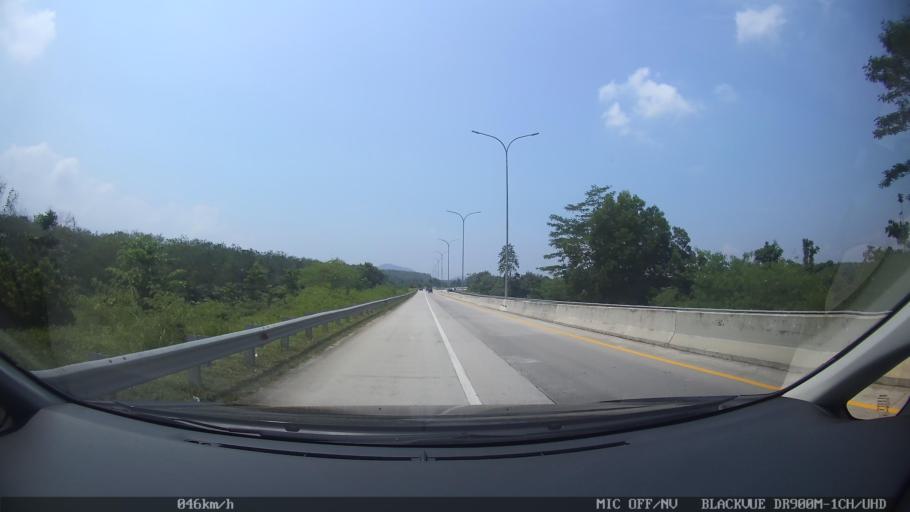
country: ID
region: Lampung
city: Kedaton
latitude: -5.3610
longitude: 105.3277
